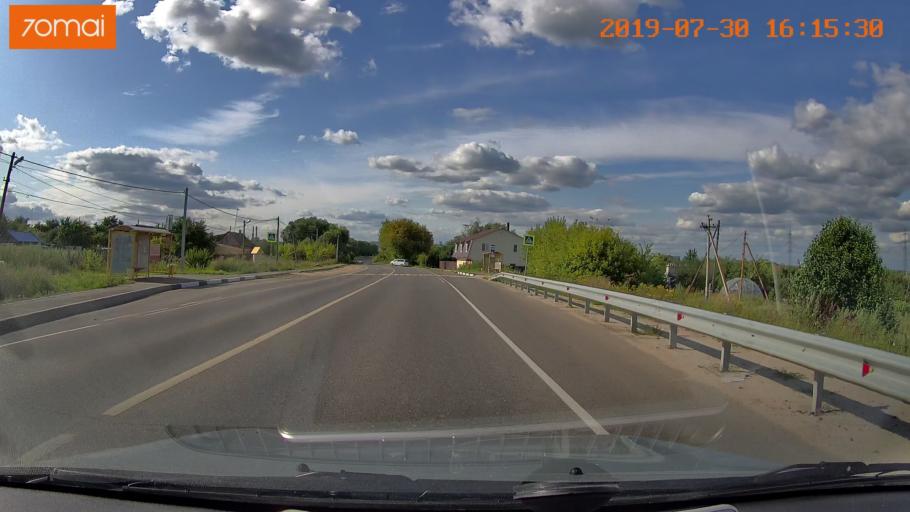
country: RU
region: Moskovskaya
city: Voskresensk
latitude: 55.2967
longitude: 38.6670
